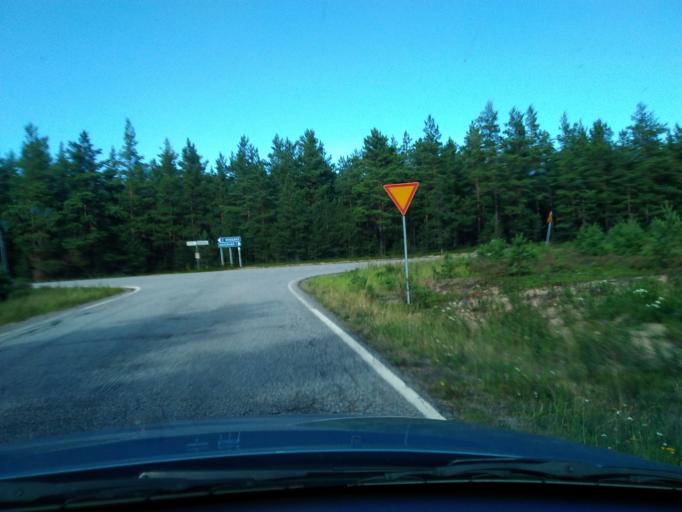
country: FI
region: Uusimaa
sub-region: Raaseporin
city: Ekenaes
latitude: 59.8821
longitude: 23.2059
